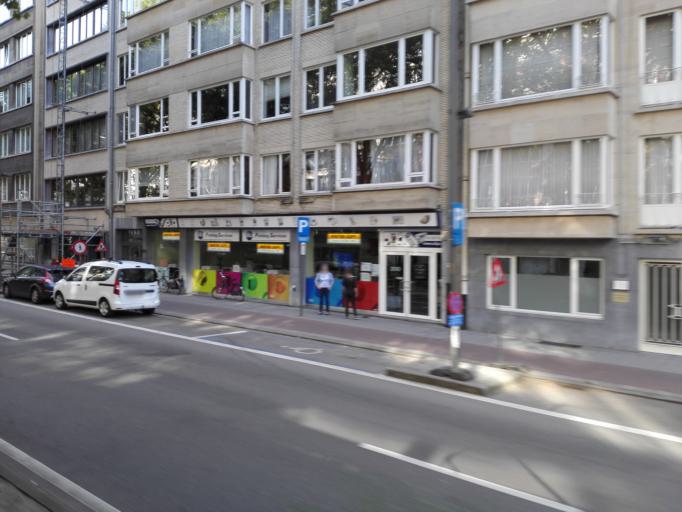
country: BE
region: Flanders
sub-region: Provincie Antwerpen
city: Antwerpen
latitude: 51.2036
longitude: 4.4112
